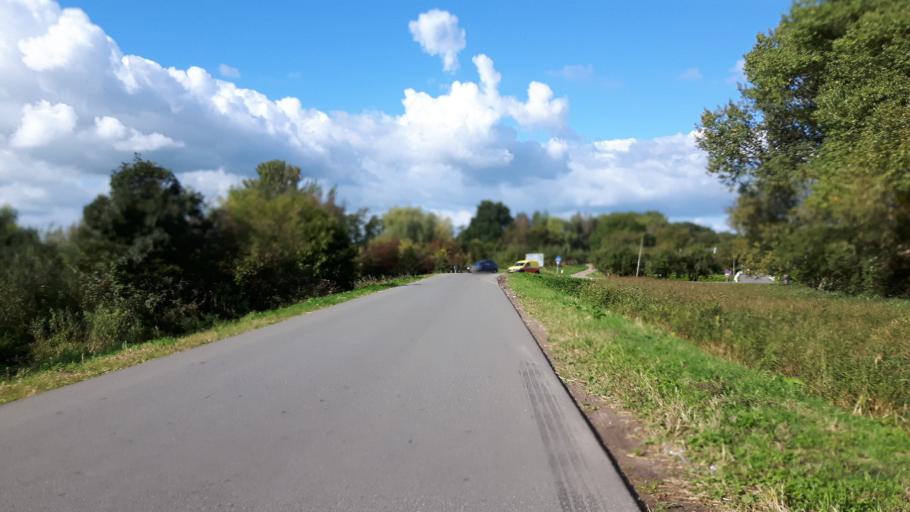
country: NL
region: South Holland
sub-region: Gemeente Leerdam
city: Leerdam
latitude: 51.8626
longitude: 5.0632
